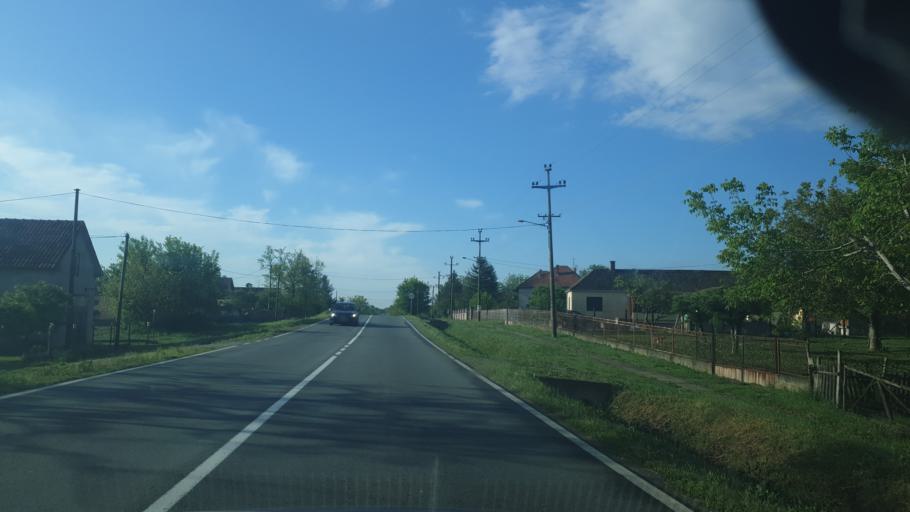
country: RS
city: Stubline
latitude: 44.5895
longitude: 20.1486
